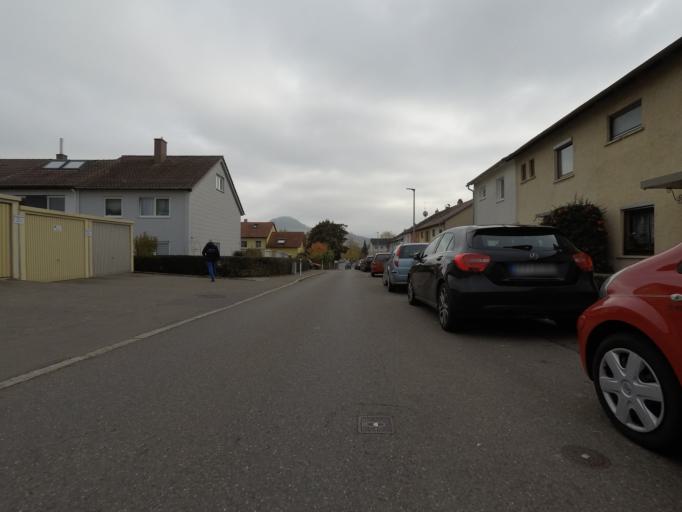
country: DE
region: Baden-Wuerttemberg
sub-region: Tuebingen Region
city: Reutlingen
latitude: 48.5079
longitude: 9.2057
